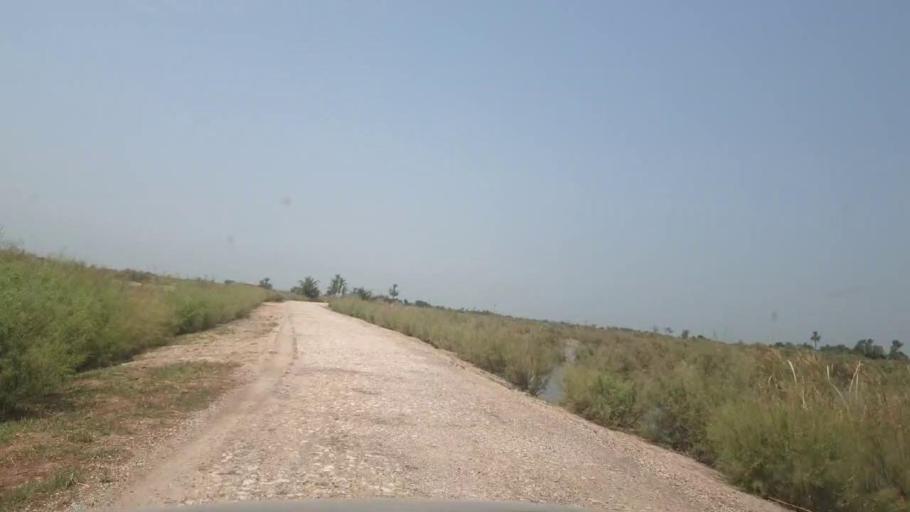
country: PK
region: Sindh
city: Lakhi
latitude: 27.8442
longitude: 68.6268
